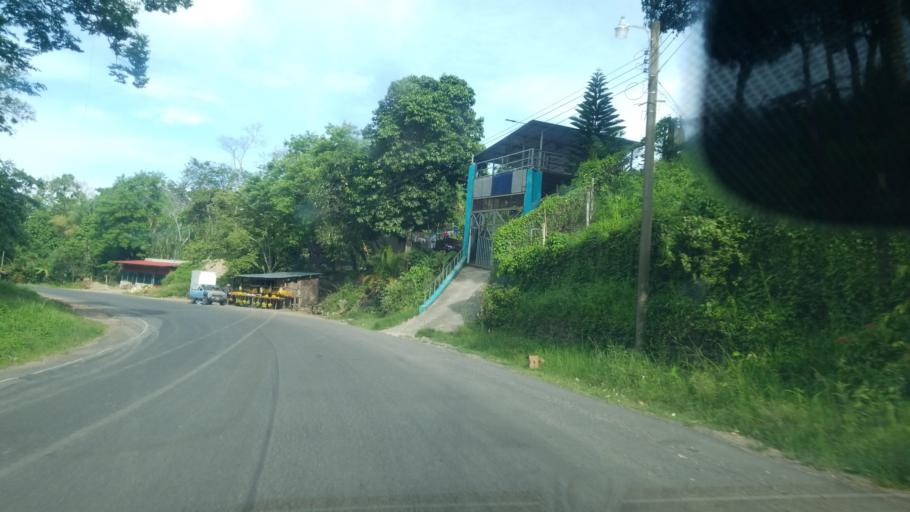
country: HN
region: Santa Barbara
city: Trinidad
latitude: 15.1780
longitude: -88.2714
